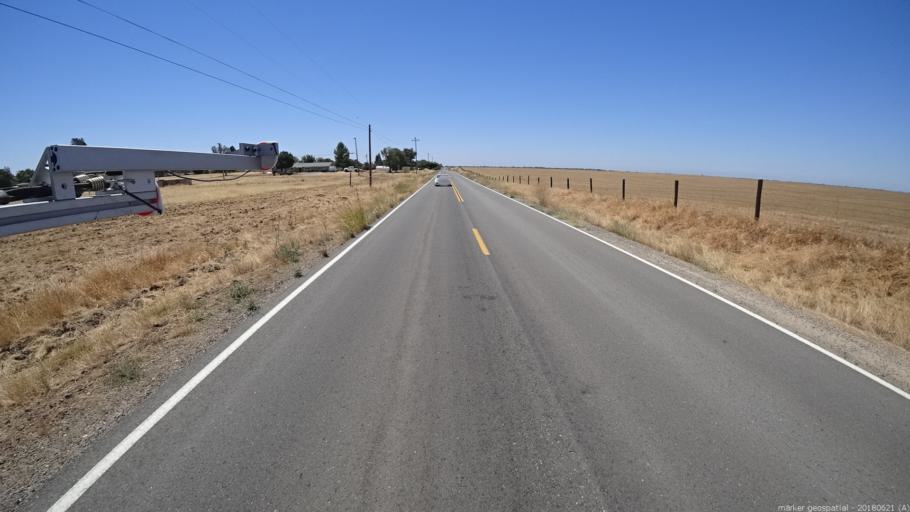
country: US
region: California
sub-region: Madera County
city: Bonadelle Ranchos-Madera Ranchos
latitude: 37.0042
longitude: -119.8937
